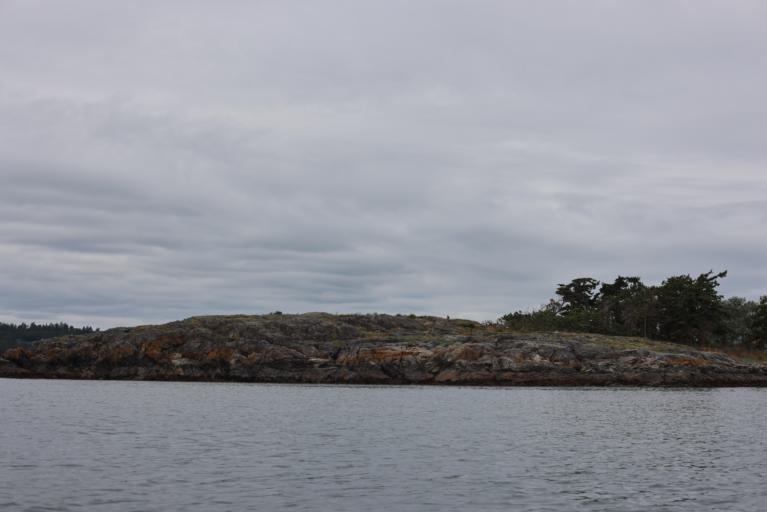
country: CA
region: British Columbia
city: Oak Bay
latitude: 48.4484
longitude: -123.2776
